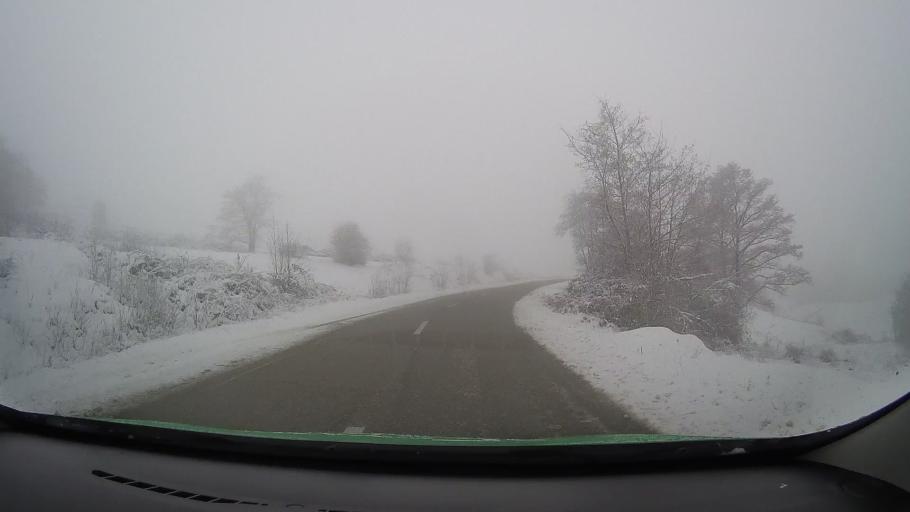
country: RO
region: Hunedoara
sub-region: Comuna Unirea
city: Unirea
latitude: 45.6643
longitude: 22.9142
